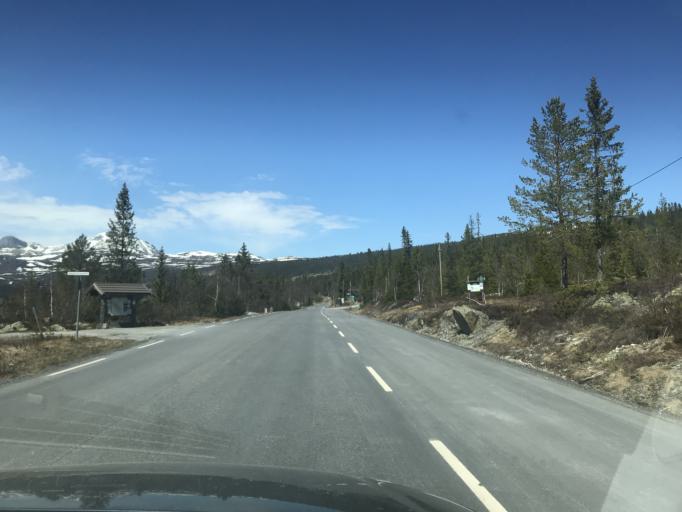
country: NO
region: Telemark
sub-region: Tinn
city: Rjukan
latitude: 59.7795
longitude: 8.7712
